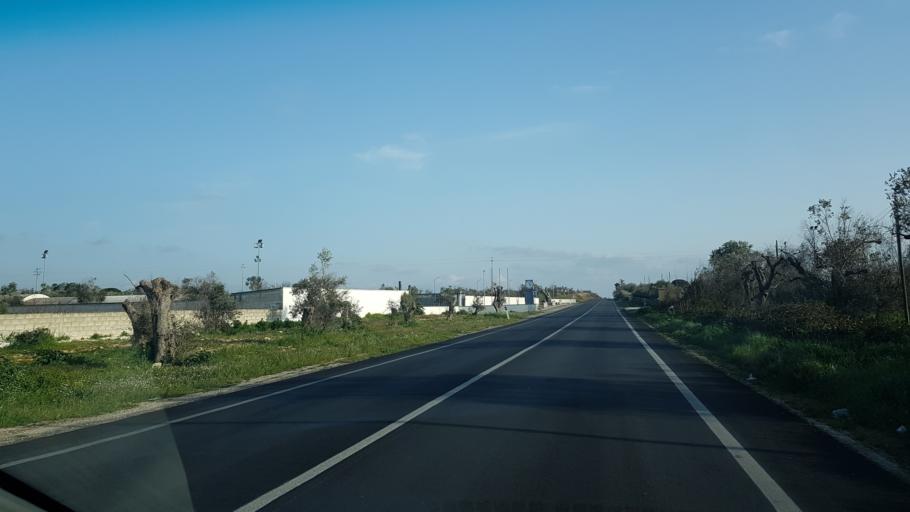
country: IT
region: Apulia
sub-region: Provincia di Lecce
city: Squinzano
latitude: 40.4209
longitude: 18.0584
